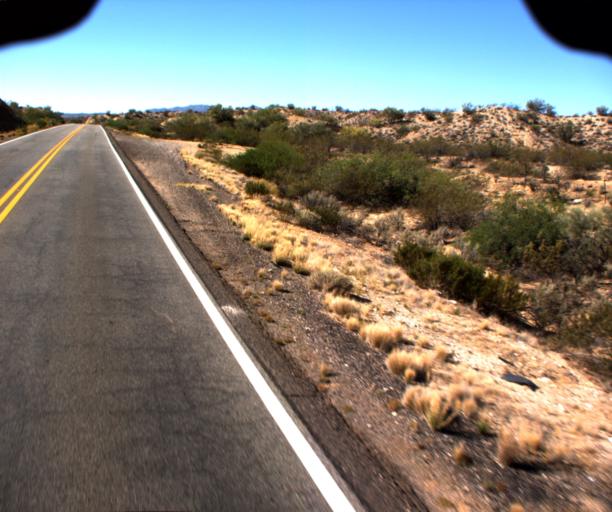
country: US
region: Arizona
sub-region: Yavapai County
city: Bagdad
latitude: 34.7806
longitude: -113.6228
